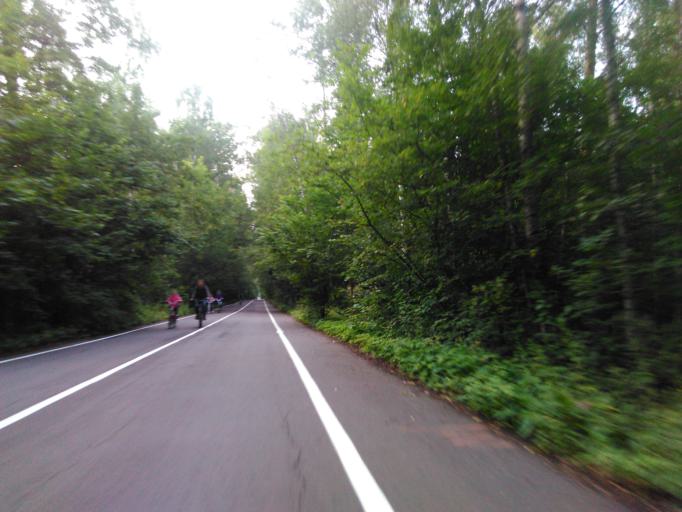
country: RU
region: Moscow
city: Babushkin
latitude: 55.8430
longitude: 37.7266
